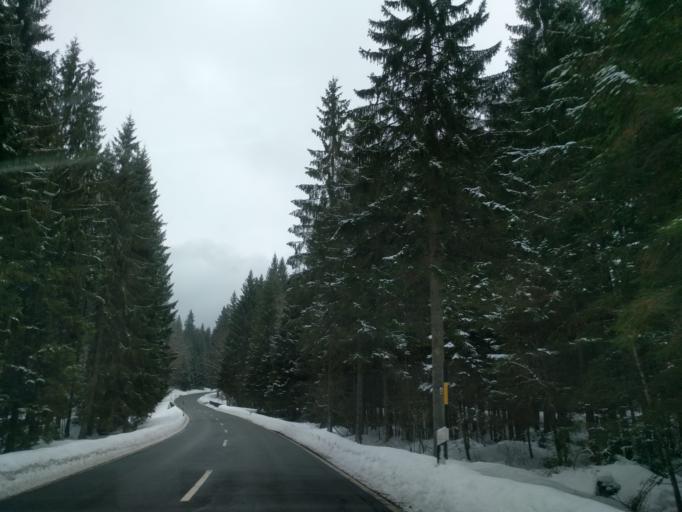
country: DE
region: Bavaria
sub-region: Lower Bavaria
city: Lindberg
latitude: 49.0524
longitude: 13.2860
